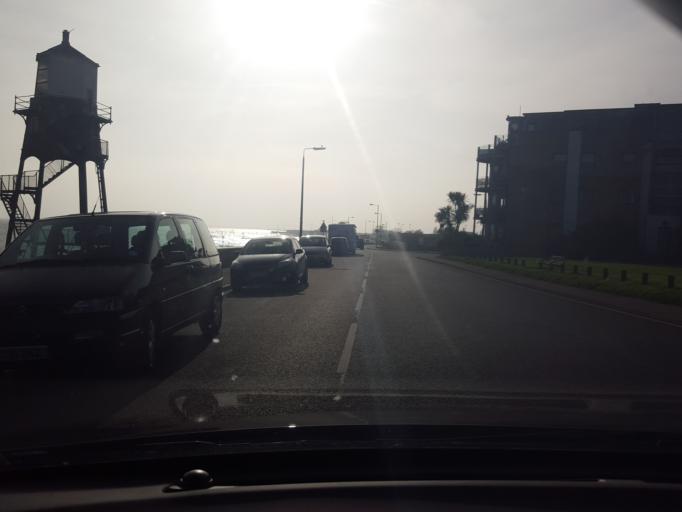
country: GB
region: England
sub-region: Essex
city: Dovercourt
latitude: 51.9309
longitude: 1.2756
